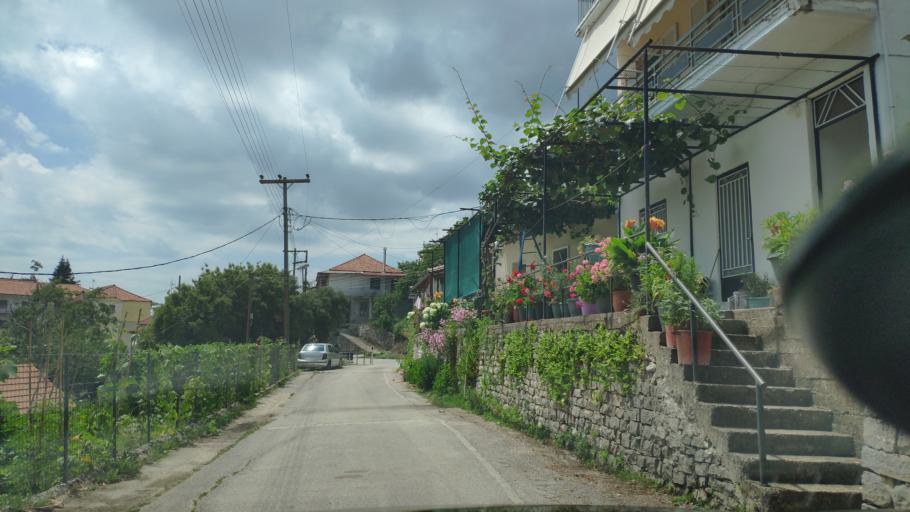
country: GR
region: Epirus
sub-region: Nomos Artas
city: Agios Dimitrios
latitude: 39.3239
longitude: 20.9972
